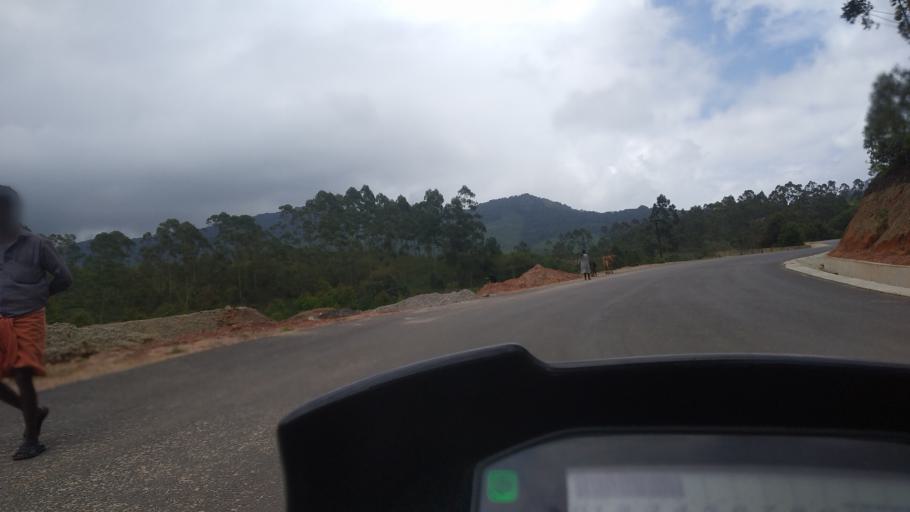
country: IN
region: Kerala
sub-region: Idukki
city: Munnar
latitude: 10.0509
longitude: 77.1107
